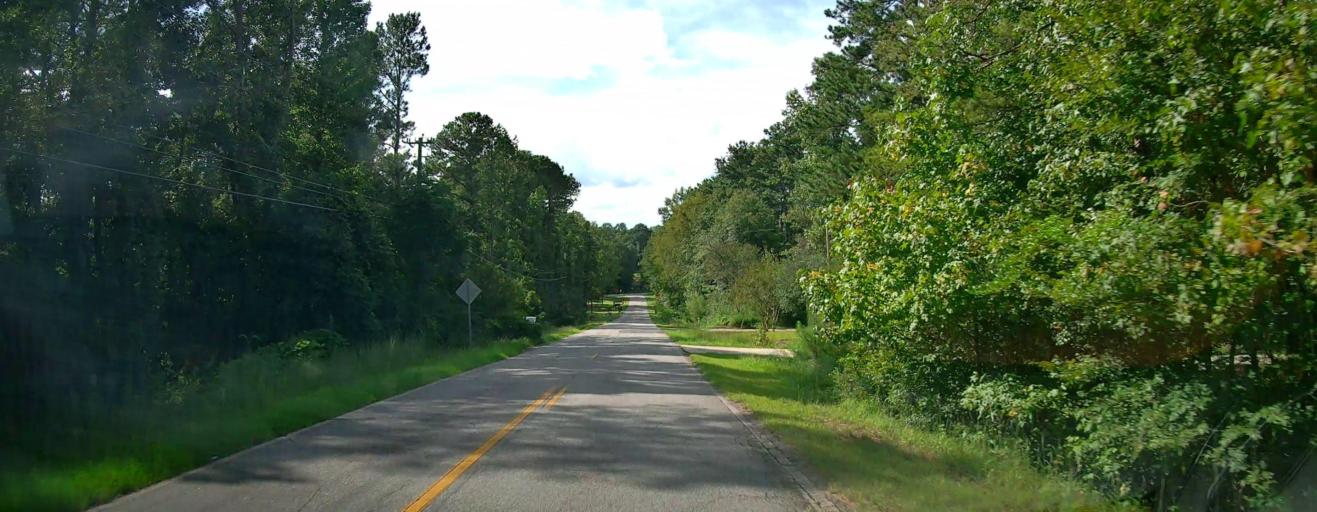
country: US
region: Alabama
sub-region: Russell County
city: Phenix City
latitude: 32.6055
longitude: -84.9785
